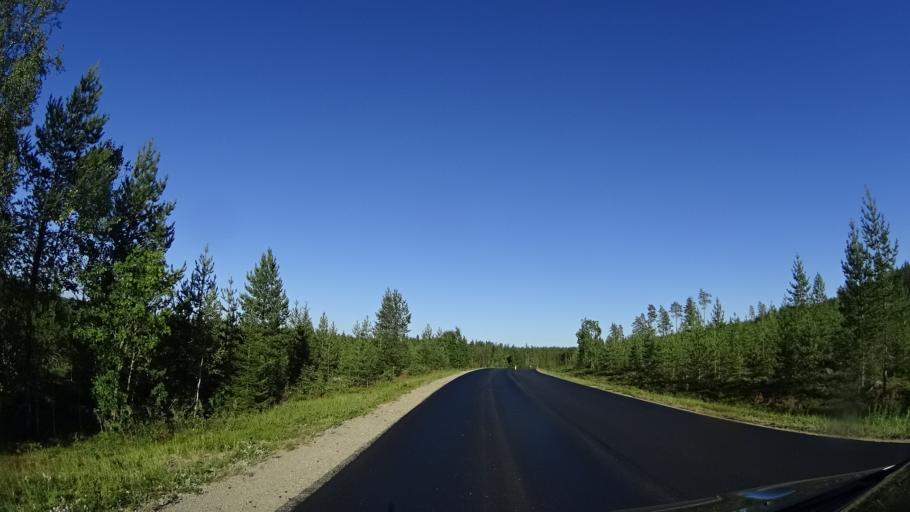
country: FI
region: North Karelia
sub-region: Pielisen Karjala
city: Valtimo
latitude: 63.5600
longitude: 28.6117
